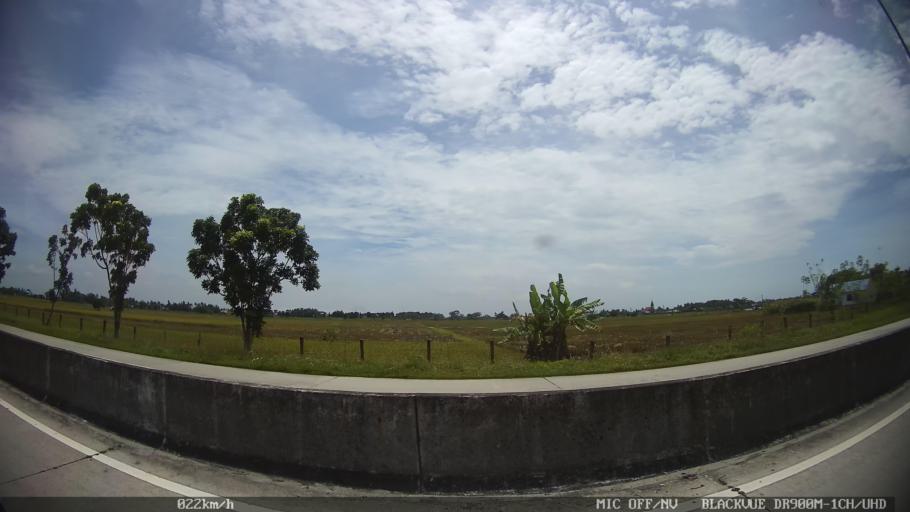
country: ID
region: North Sumatra
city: Perbaungan
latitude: 3.5398
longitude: 98.8924
